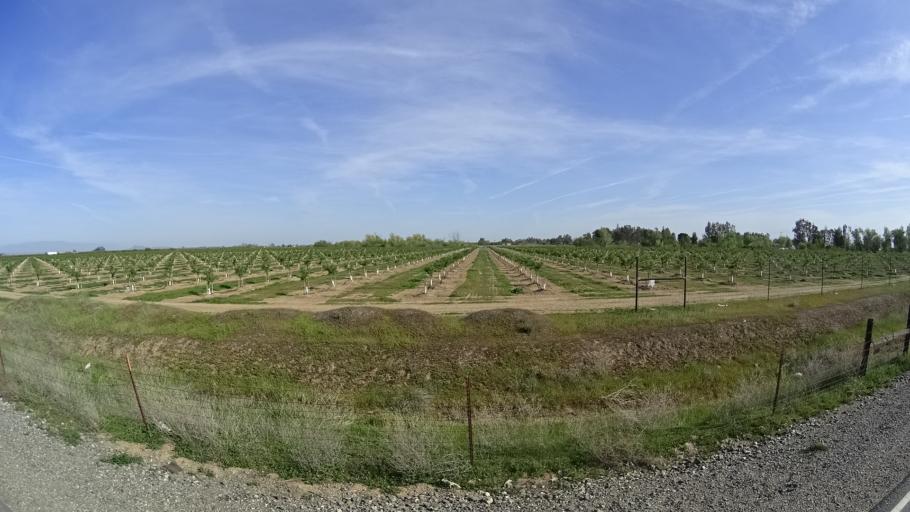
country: US
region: California
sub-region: Glenn County
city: Willows
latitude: 39.6240
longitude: -122.2000
